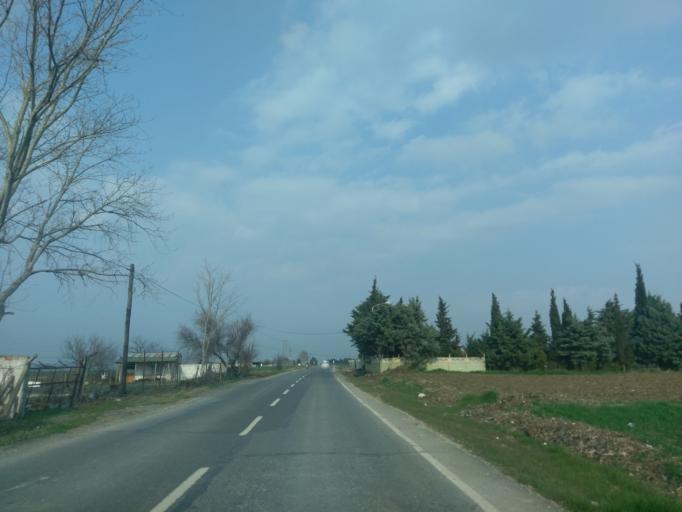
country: TR
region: Istanbul
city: Silivri
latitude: 41.0936
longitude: 28.2755
